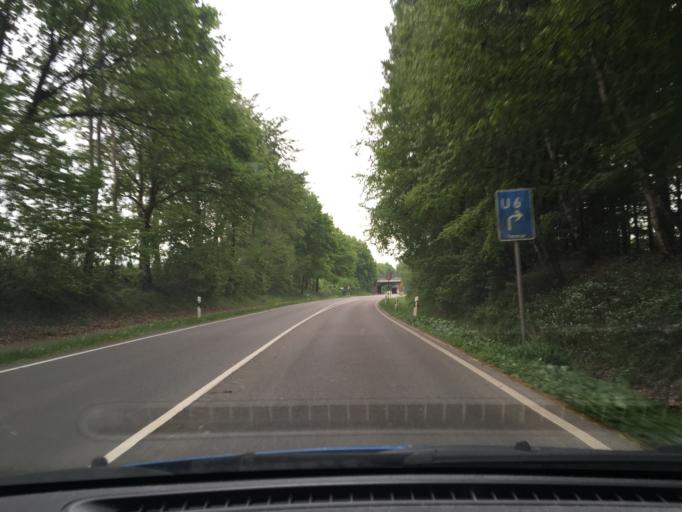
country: DE
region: Lower Saxony
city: Brackel
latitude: 53.3076
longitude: 10.0667
